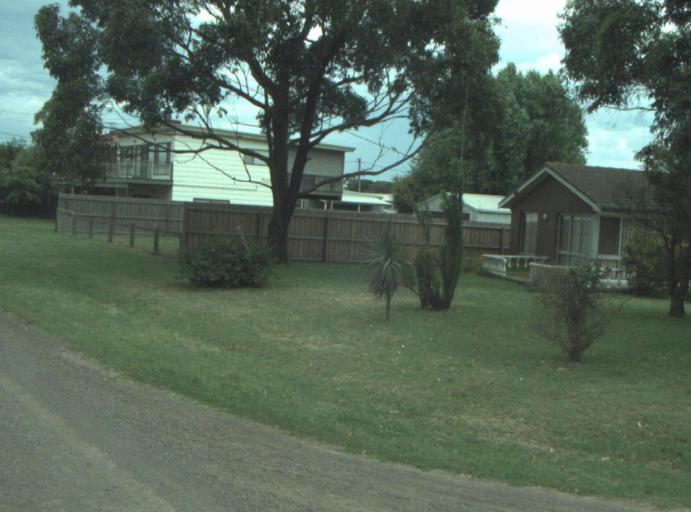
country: AU
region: Victoria
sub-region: Greater Geelong
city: Clifton Springs
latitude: -38.1205
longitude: 144.6690
